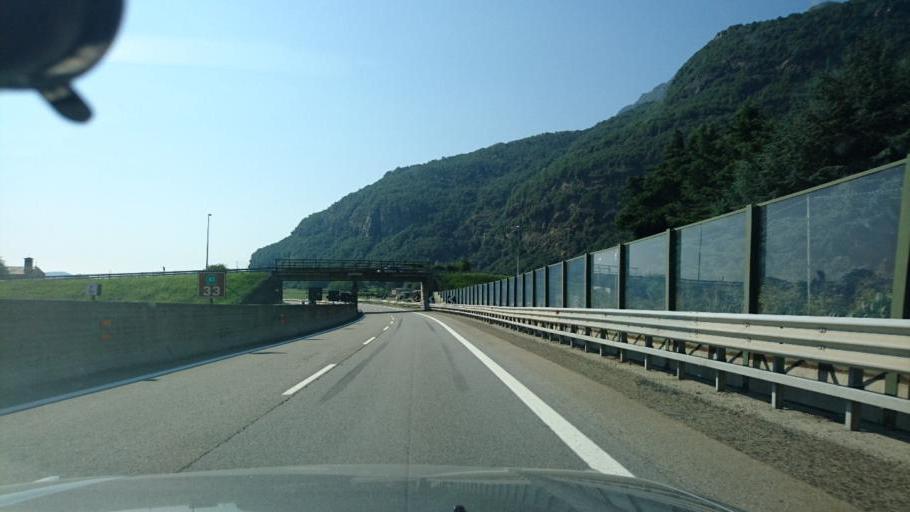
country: IT
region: Piedmont
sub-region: Provincia di Torino
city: Tavagnasco
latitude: 45.5455
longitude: 7.8242
